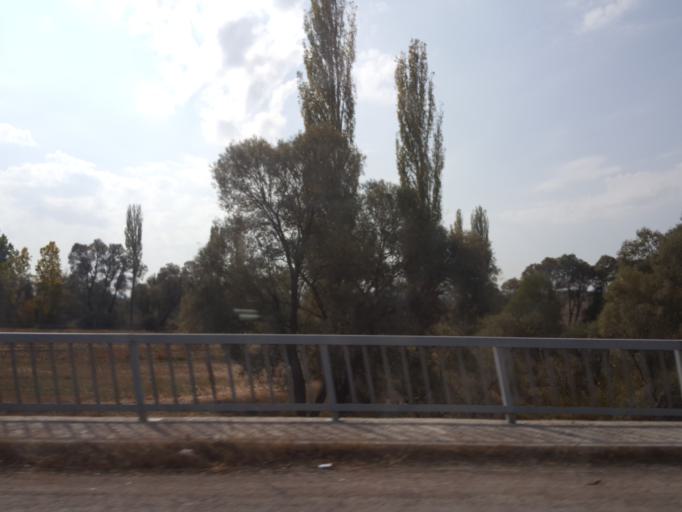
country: TR
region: Corum
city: Alaca
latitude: 40.1751
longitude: 34.8944
